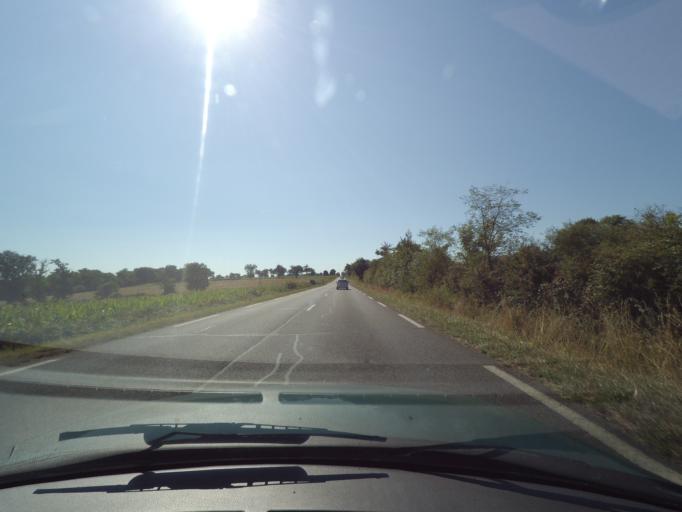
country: FR
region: Limousin
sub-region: Departement de la Haute-Vienne
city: Peyrat-de-Bellac
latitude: 46.1431
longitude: 0.9747
